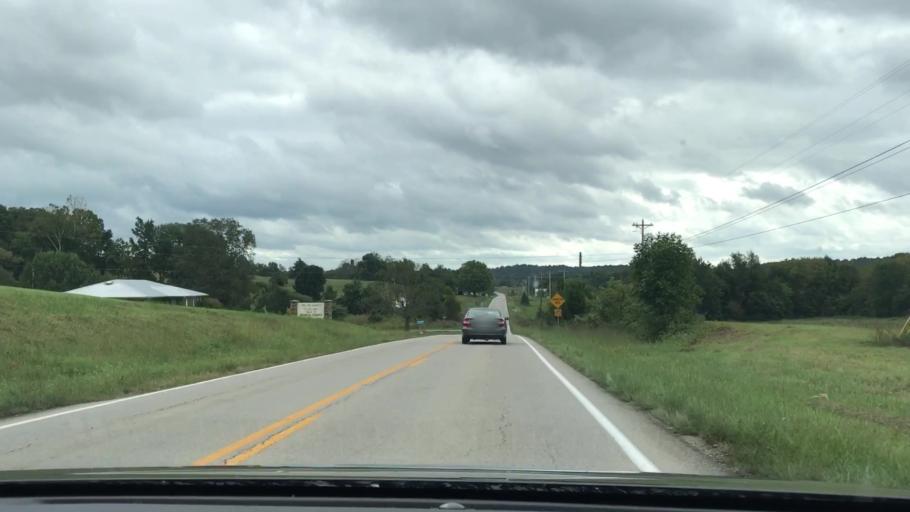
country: US
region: Kentucky
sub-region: Metcalfe County
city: Edmonton
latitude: 36.9044
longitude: -85.7534
